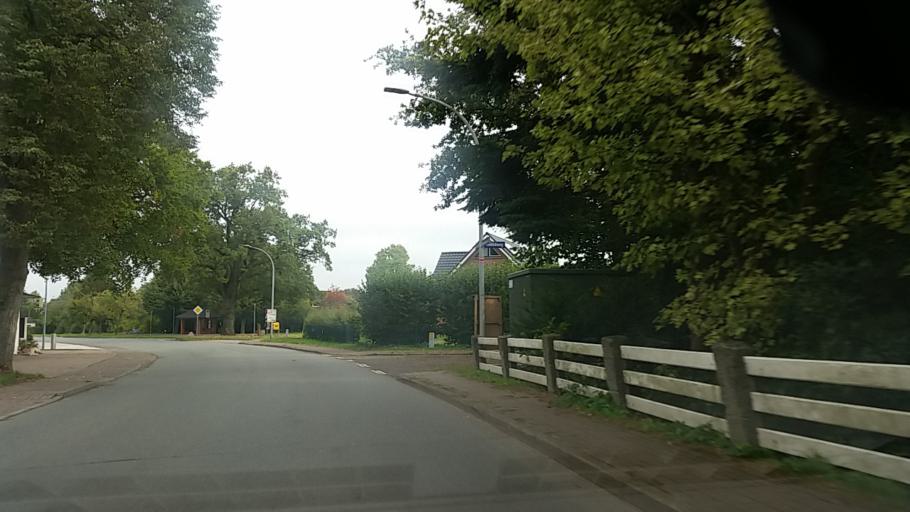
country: DE
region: Schleswig-Holstein
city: Schmalfeld
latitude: 53.8733
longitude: 9.9856
